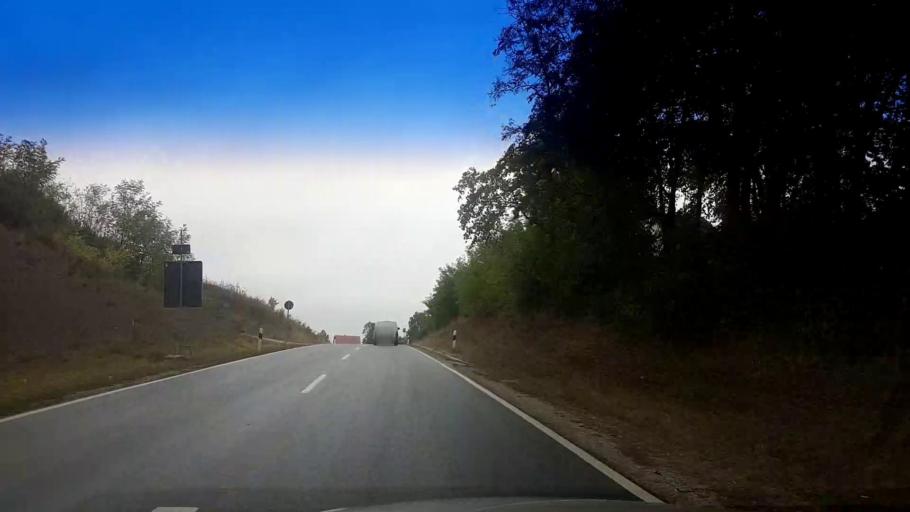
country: DE
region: Bavaria
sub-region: Upper Franconia
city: Buttenheim
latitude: 49.7991
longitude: 11.0339
